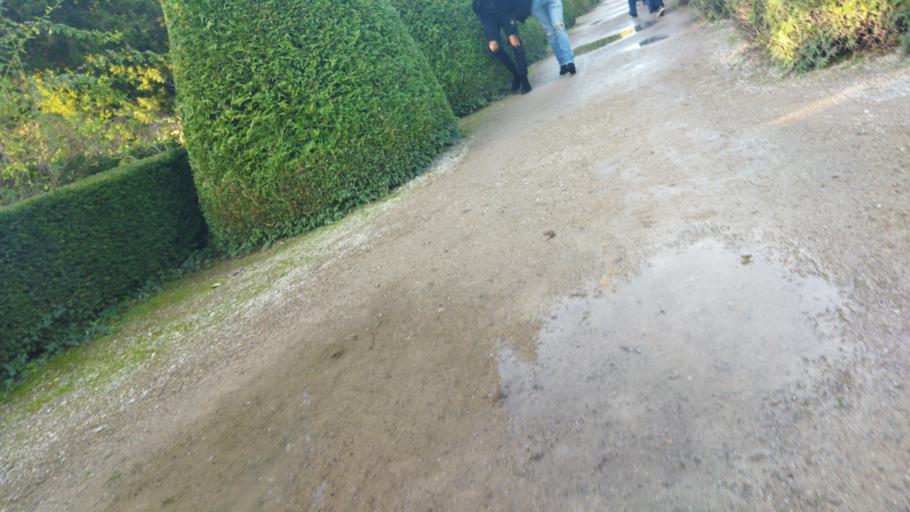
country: DE
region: Baden-Wuerttemberg
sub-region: Karlsruhe Region
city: Schwetzingen
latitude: 49.3814
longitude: 8.5654
